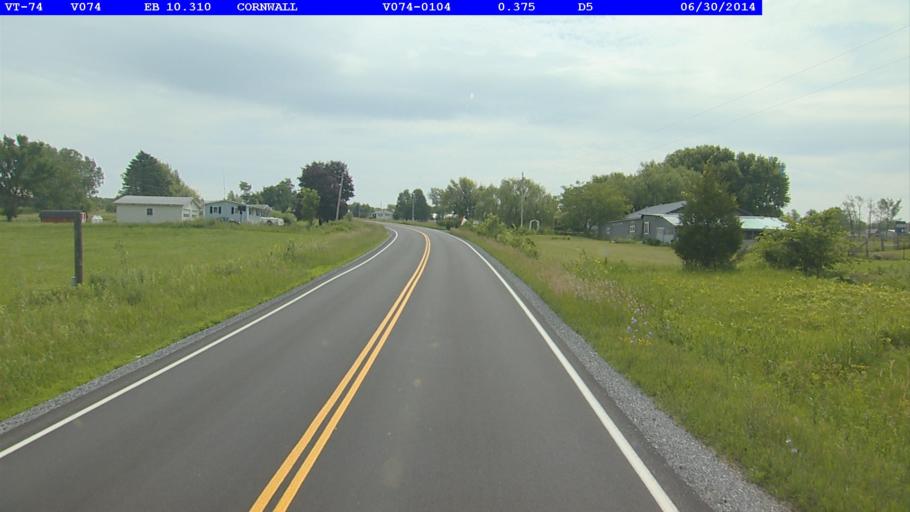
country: US
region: Vermont
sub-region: Addison County
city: Middlebury (village)
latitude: 43.9425
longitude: -73.2504
